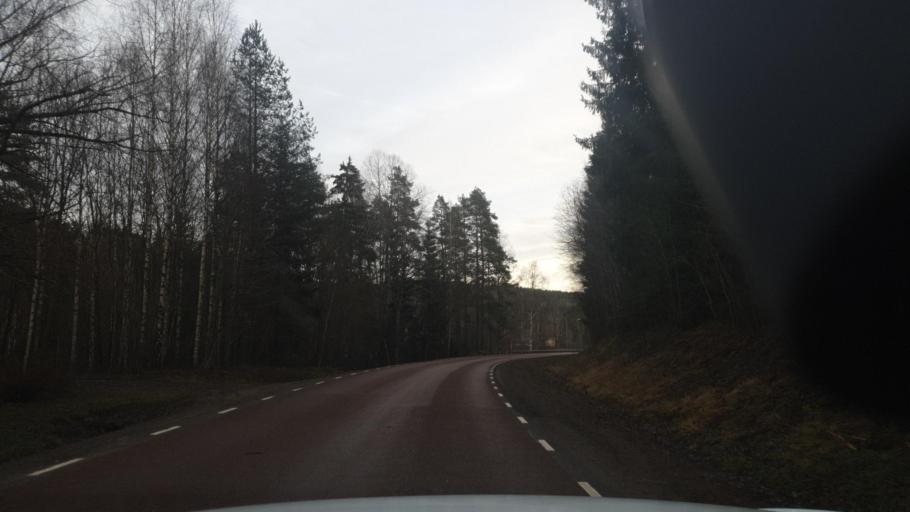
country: NO
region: Hedmark
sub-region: Eidskog
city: Skotterud
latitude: 59.8185
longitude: 12.0063
